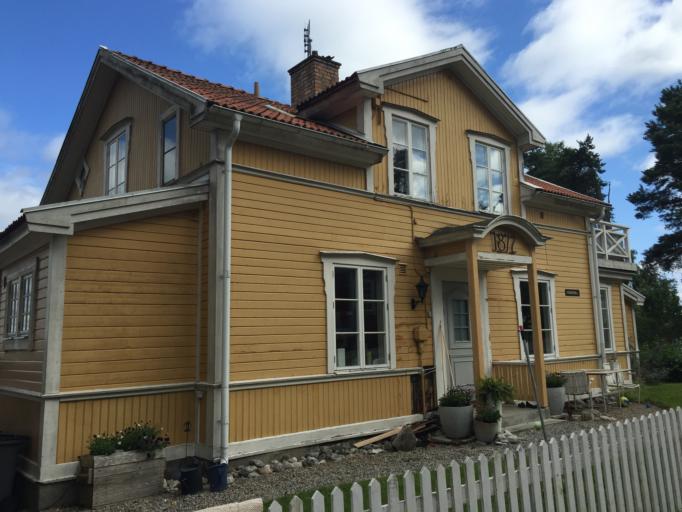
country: SE
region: Soedermanland
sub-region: Trosa Kommun
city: Trosa
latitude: 58.9689
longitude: 17.7167
